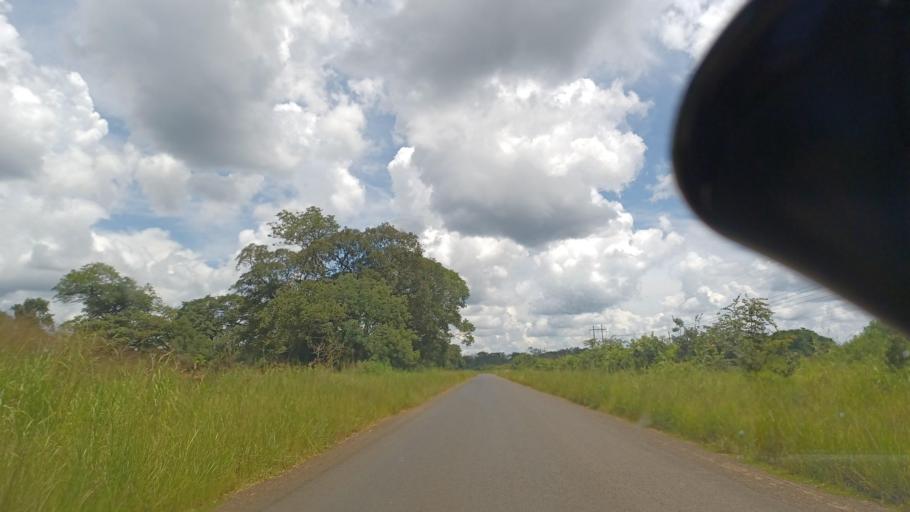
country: ZM
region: North-Western
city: Solwezi
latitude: -12.4305
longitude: 26.2141
